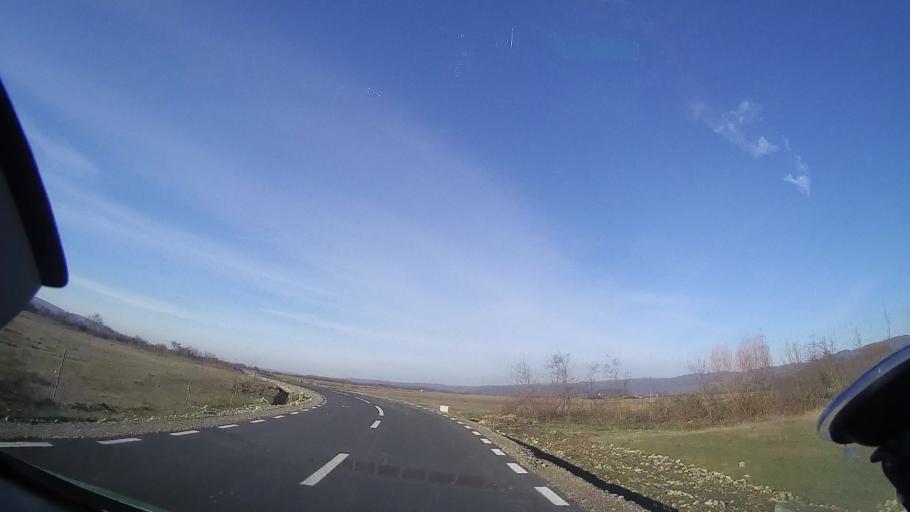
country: RO
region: Bihor
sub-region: Comuna Auseu
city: Auseu
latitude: 47.0121
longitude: 22.4993
